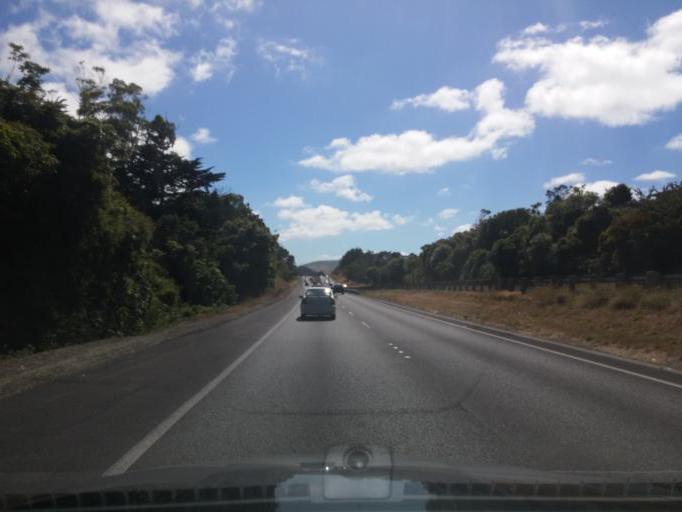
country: NZ
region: Wellington
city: Petone
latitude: -41.2124
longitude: 174.8144
